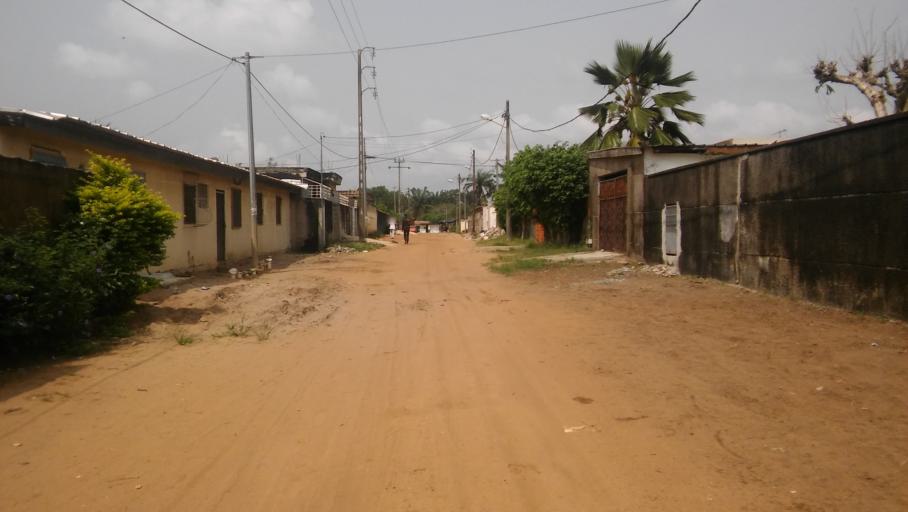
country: CI
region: Sud-Comoe
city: Grand-Bassam
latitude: 5.2180
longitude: -3.7294
